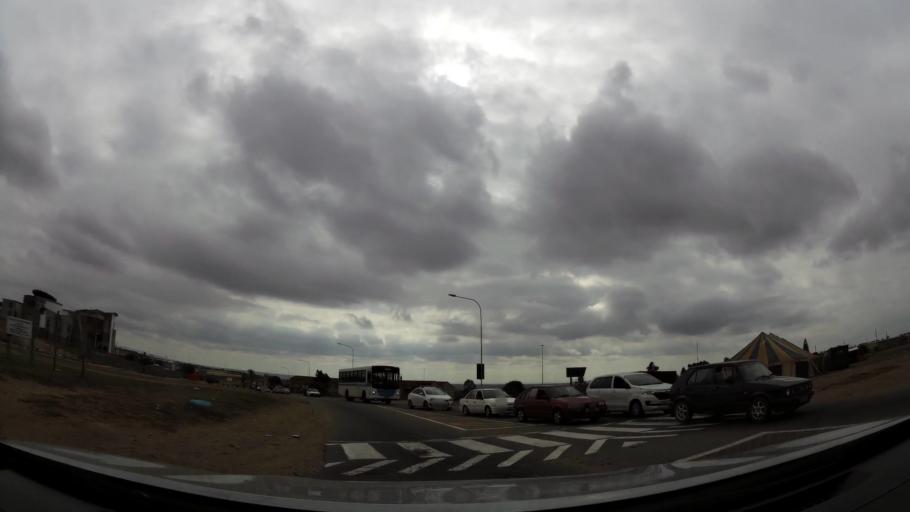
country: ZA
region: Eastern Cape
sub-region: Nelson Mandela Bay Metropolitan Municipality
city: Port Elizabeth
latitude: -33.8805
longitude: 25.5639
